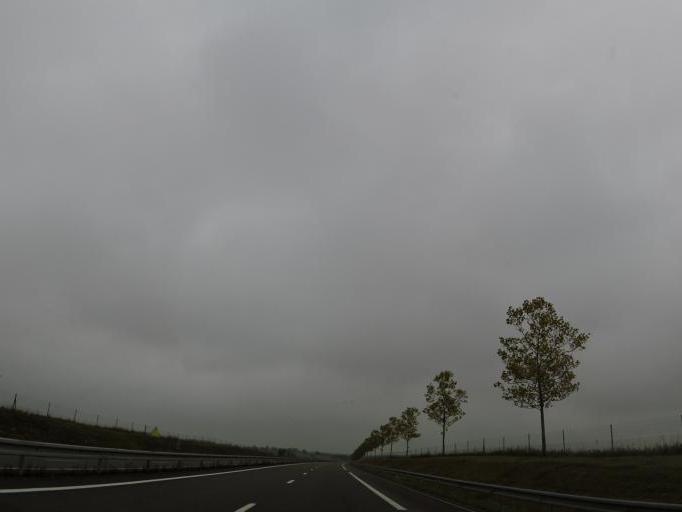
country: FR
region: Champagne-Ardenne
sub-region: Departement de la Marne
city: Suippes
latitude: 49.0464
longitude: 4.6553
